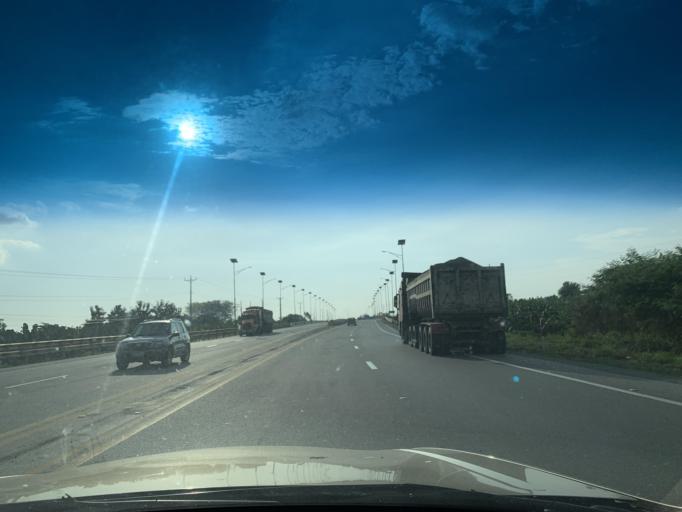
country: EC
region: Guayas
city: Naranjito
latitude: -2.2583
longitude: -79.5557
